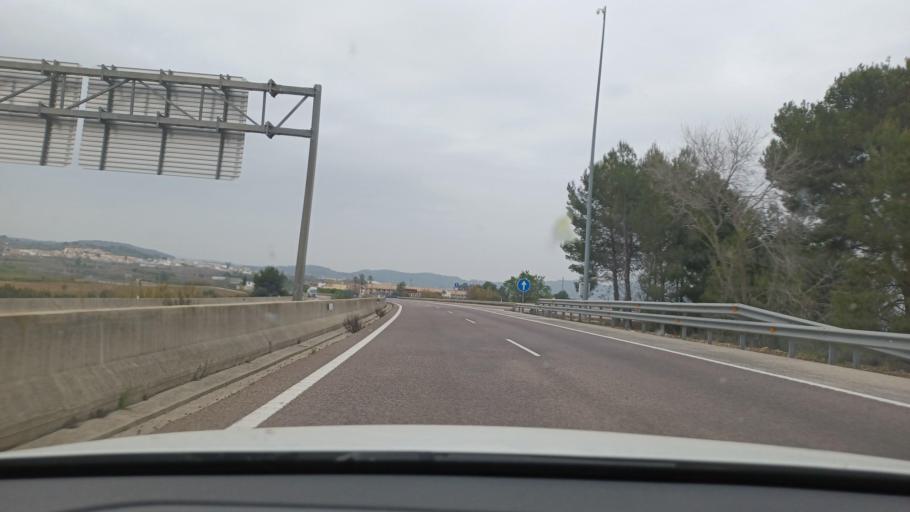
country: ES
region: Valencia
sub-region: Provincia de Valencia
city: Cerda
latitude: 38.9692
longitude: -0.5645
